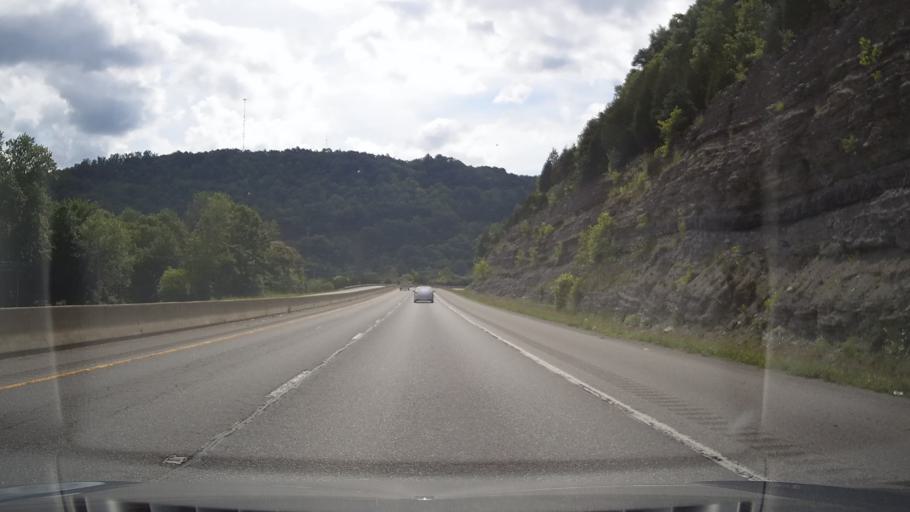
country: US
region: Kentucky
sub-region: Pike County
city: Coal Run Village
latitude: 37.5586
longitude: -82.6382
